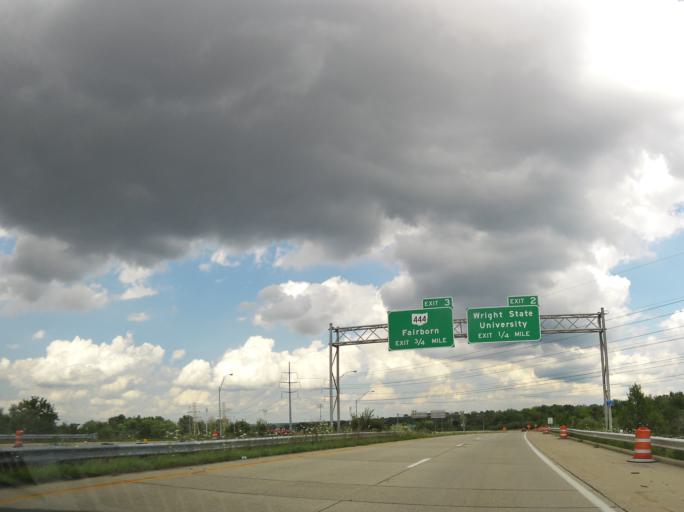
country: US
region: Ohio
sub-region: Greene County
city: Wright-Patterson AFB
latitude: 39.7807
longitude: -84.0492
